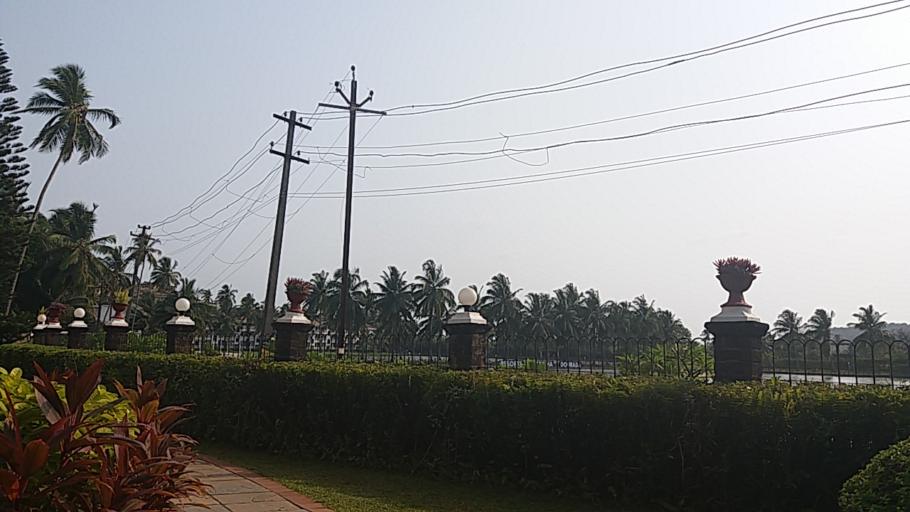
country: IN
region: Goa
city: Calangute
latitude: 15.5682
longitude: 73.7608
